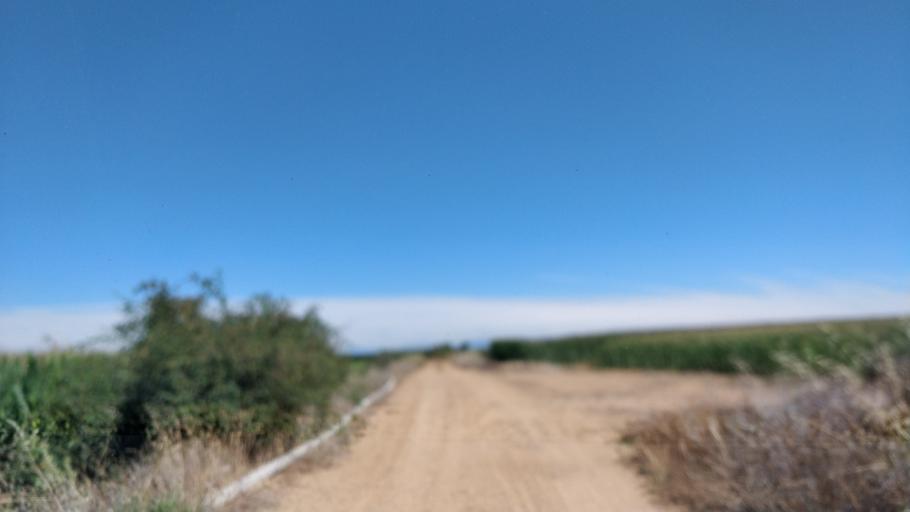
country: ES
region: Castille and Leon
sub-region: Provincia de Leon
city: Bustillo del Paramo
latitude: 42.4424
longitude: -5.8151
